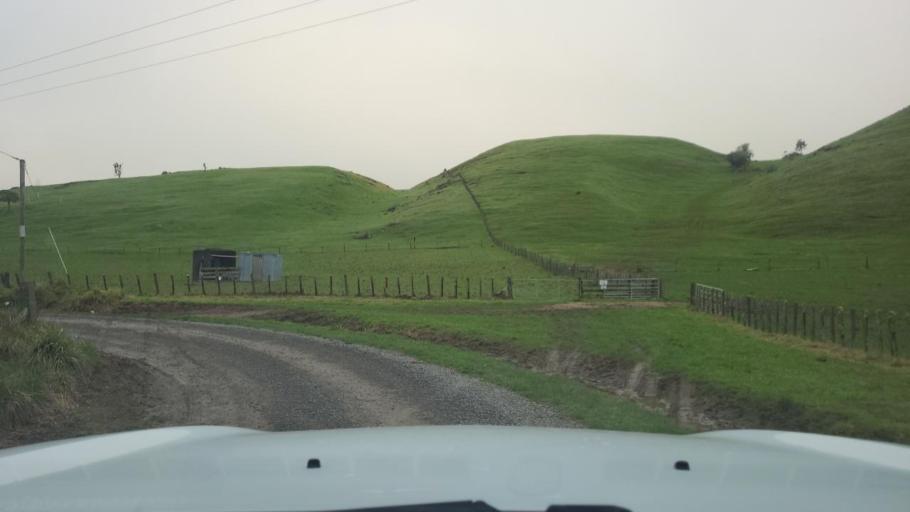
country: NZ
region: Wellington
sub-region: Masterton District
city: Masterton
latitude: -41.1349
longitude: 175.6760
